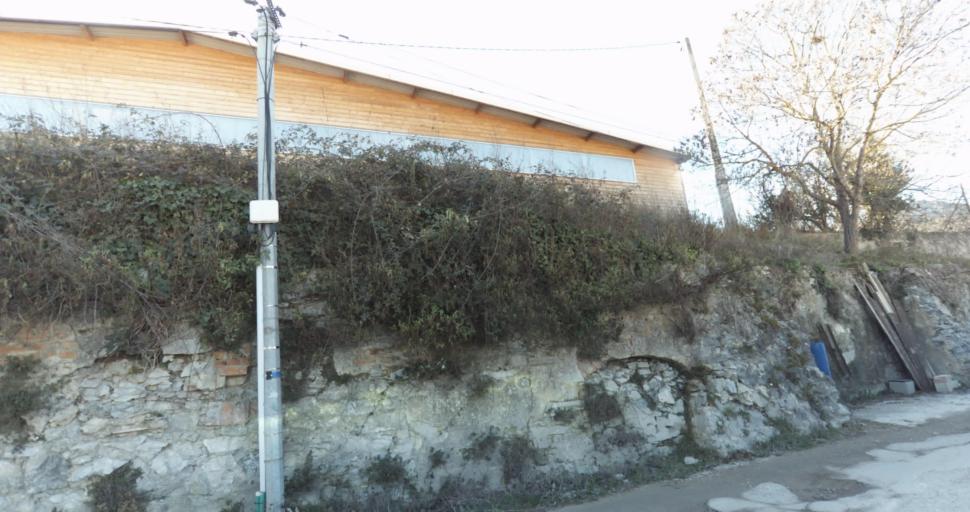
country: FR
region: Provence-Alpes-Cote d'Azur
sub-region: Departement des Bouches-du-Rhone
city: Cadolive
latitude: 43.3899
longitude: 5.5558
